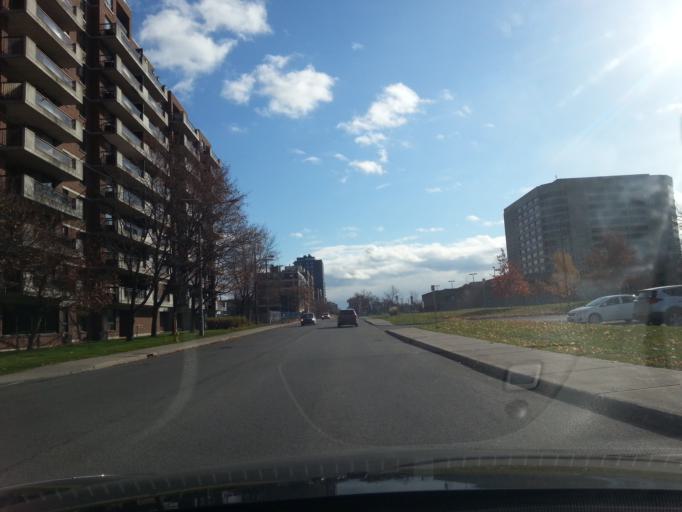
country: CA
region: Ontario
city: Ottawa
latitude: 45.4100
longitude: -75.7346
